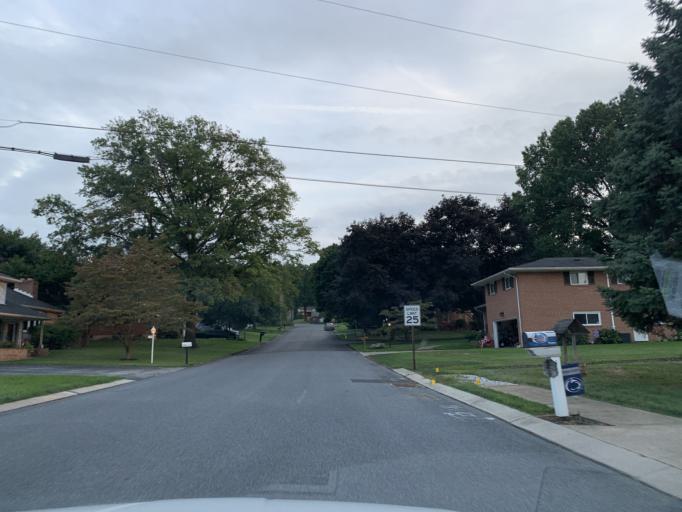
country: US
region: Pennsylvania
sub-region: York County
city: Emigsville
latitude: 40.0057
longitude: -76.7274
